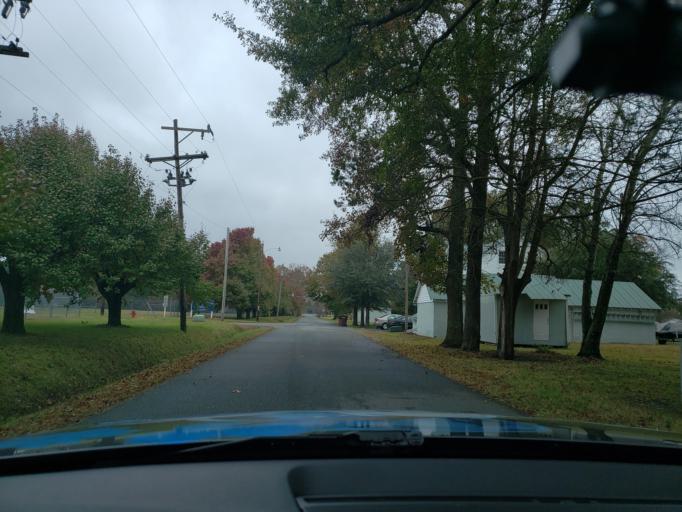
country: US
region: Virginia
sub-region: City of Chesapeake
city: Chesapeake
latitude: 36.7080
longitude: -76.1274
